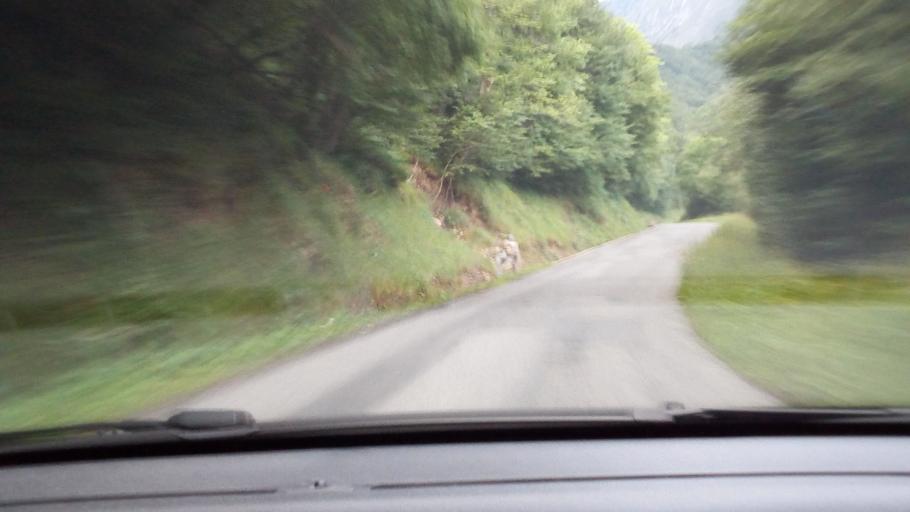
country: FR
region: Midi-Pyrenees
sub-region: Departement des Hautes-Pyrenees
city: Cauterets
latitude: 42.9454
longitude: -0.2149
